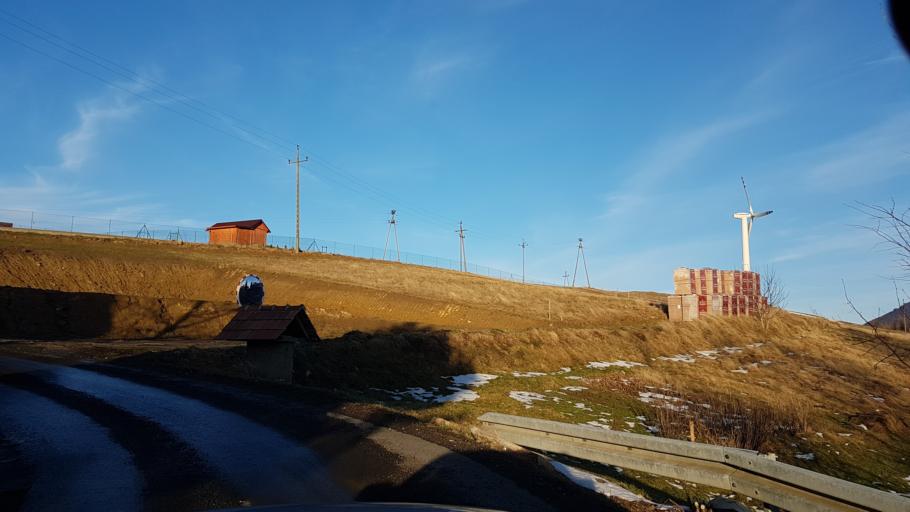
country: PL
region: Lesser Poland Voivodeship
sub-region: Powiat nowosadecki
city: Rytro
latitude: 49.4916
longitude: 20.6588
